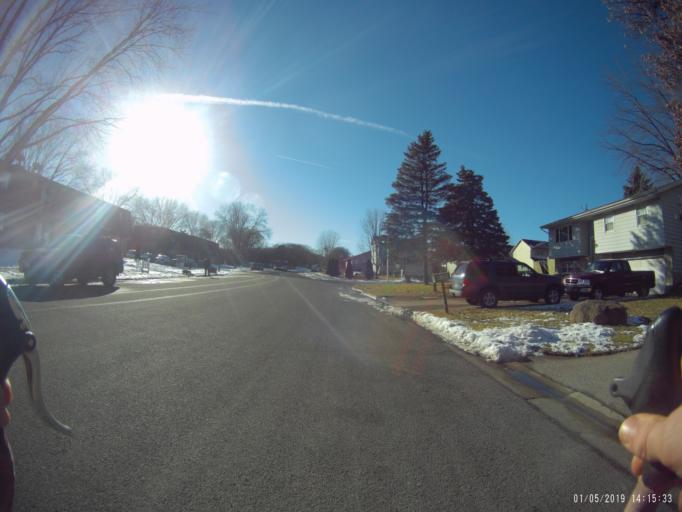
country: US
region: Wisconsin
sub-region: Dane County
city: Shorewood Hills
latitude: 43.0259
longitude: -89.4549
